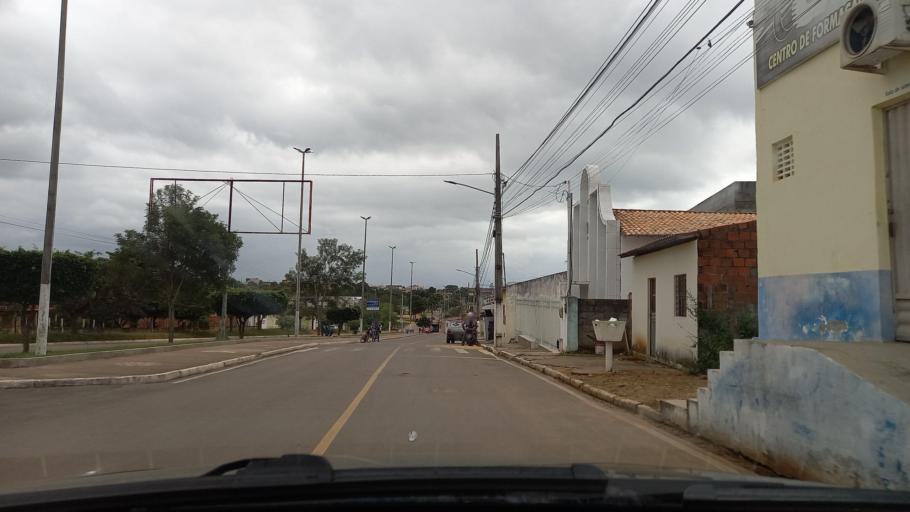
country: BR
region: Sergipe
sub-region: Caninde De Sao Francisco
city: Caninde de Sao Francisco
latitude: -9.6730
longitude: -37.7932
